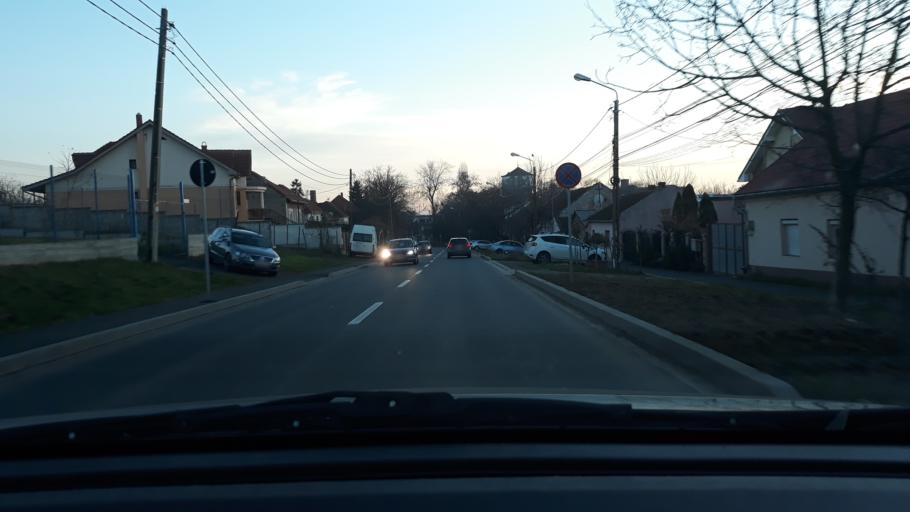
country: RO
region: Bihor
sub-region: Comuna Biharea
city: Oradea
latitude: 47.0846
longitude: 21.9272
